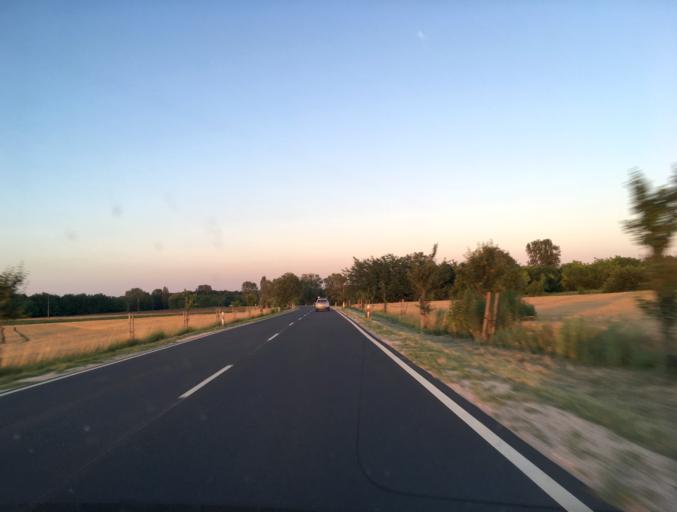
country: HU
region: Komarom-Esztergom
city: Acs
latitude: 47.7216
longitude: 18.0309
